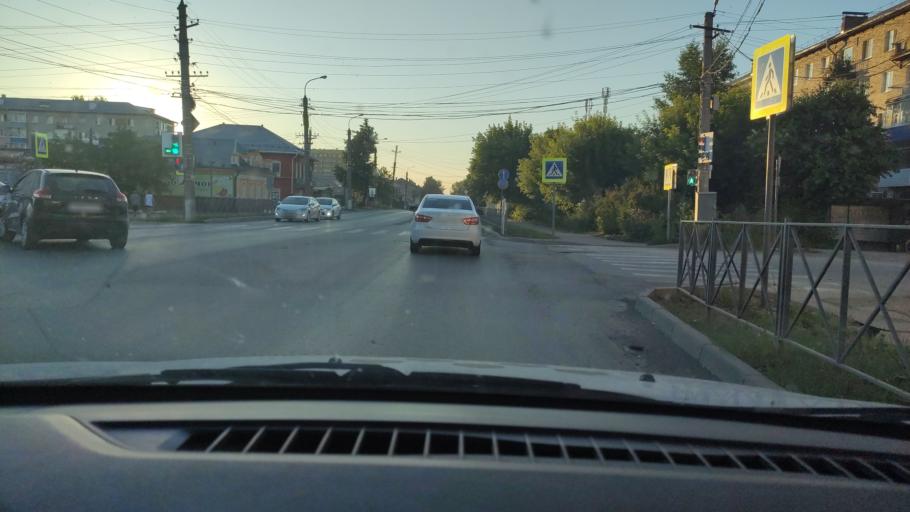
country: RU
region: Perm
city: Kungur
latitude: 57.4326
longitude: 56.9386
